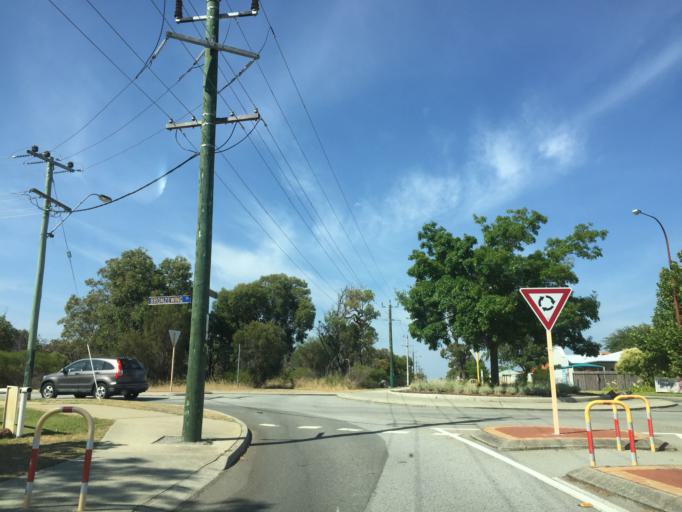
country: AU
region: Western Australia
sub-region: Gosnells
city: Thornlie
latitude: -32.0814
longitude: 115.9613
